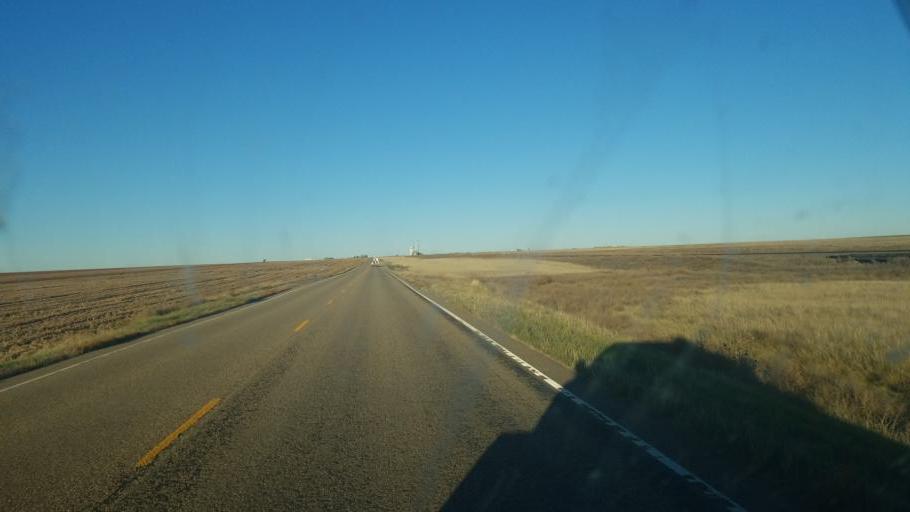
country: US
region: Colorado
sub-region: Cheyenne County
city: Cheyenne Wells
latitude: 38.8167
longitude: -102.5215
